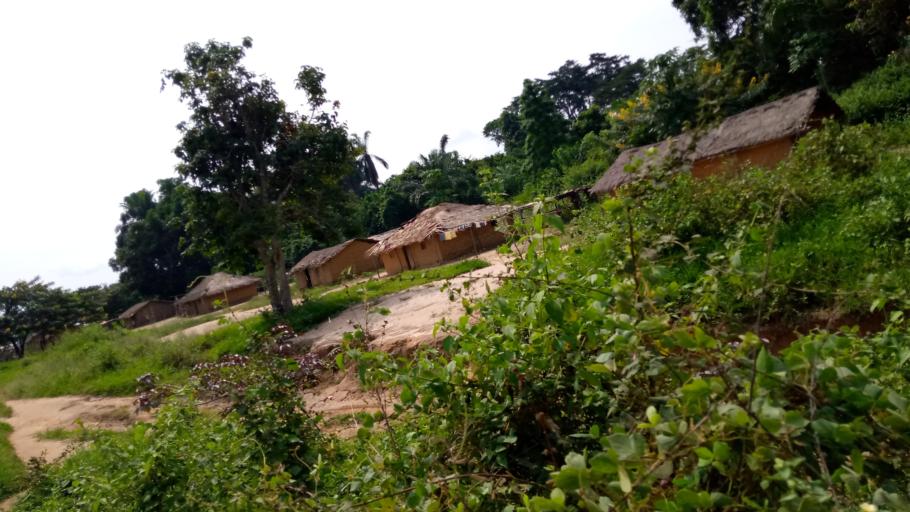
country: CD
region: Bandundu
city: Bandundu
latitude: -4.1290
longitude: 17.4114
